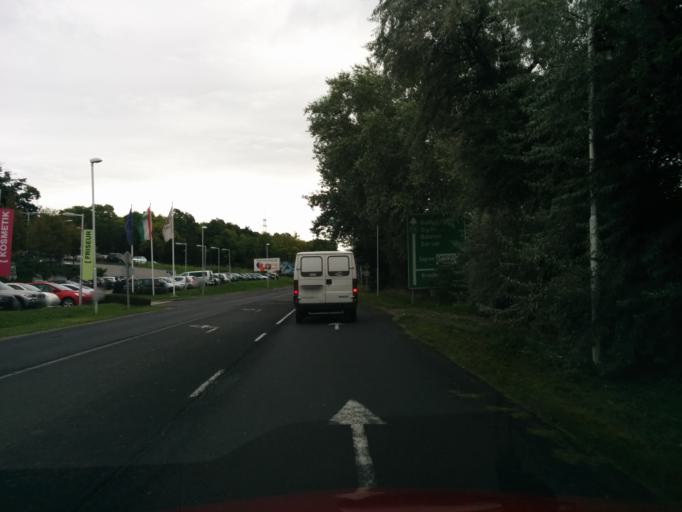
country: HU
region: Gyor-Moson-Sopron
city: Sopron
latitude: 47.7034
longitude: 16.5779
